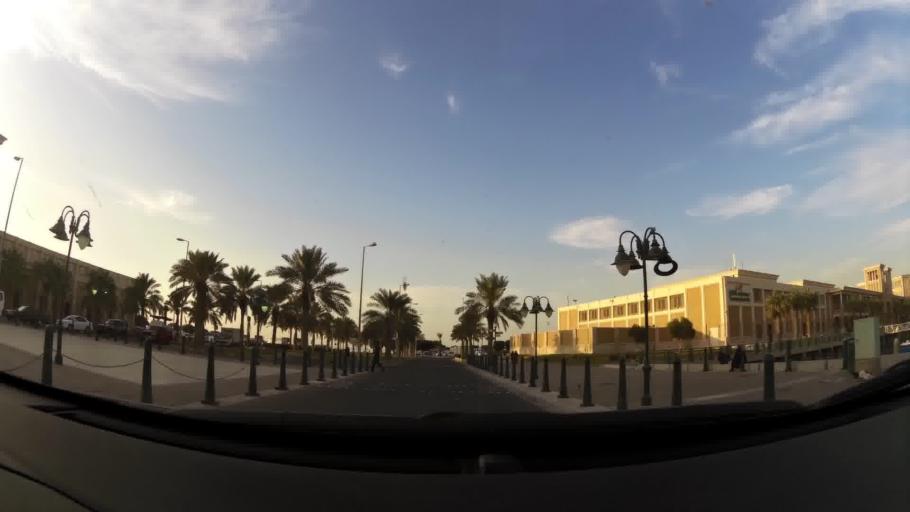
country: KW
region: Al Asimah
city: Kuwait City
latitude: 29.3871
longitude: 47.9800
